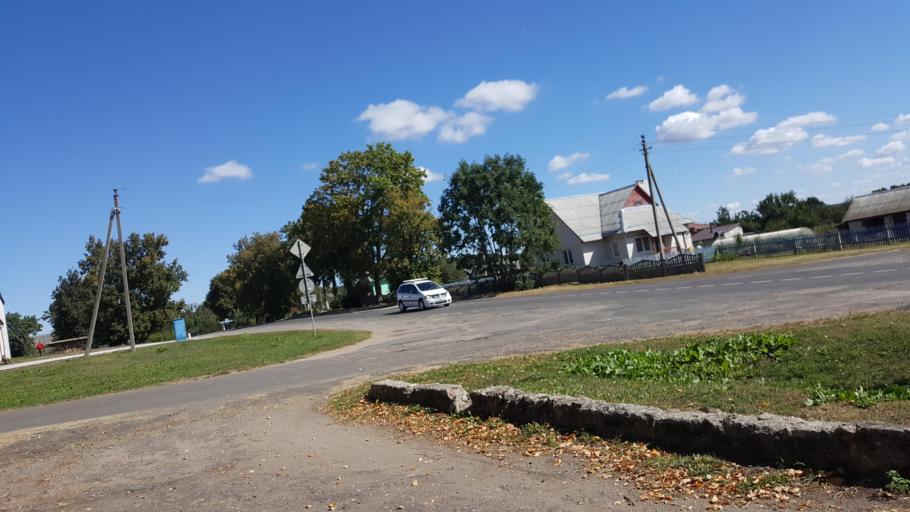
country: BY
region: Brest
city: Vysokaye
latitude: 52.3470
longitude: 23.3447
